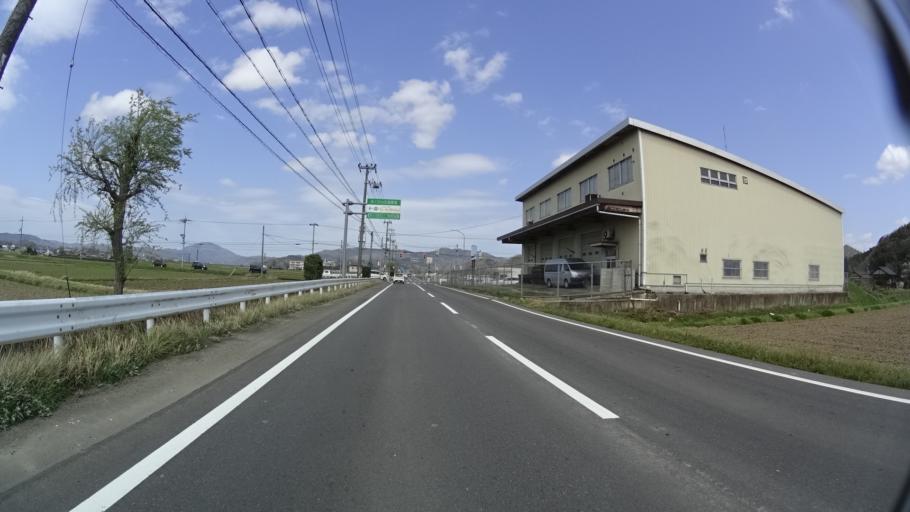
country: JP
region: Hyogo
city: Toyooka
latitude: 35.5236
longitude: 134.8399
